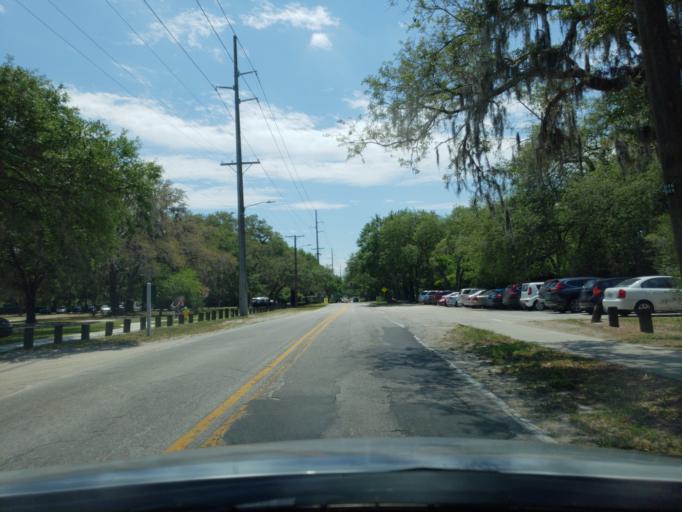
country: US
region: Florida
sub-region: Hillsborough County
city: Egypt Lake-Leto
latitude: 28.0162
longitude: -82.4678
